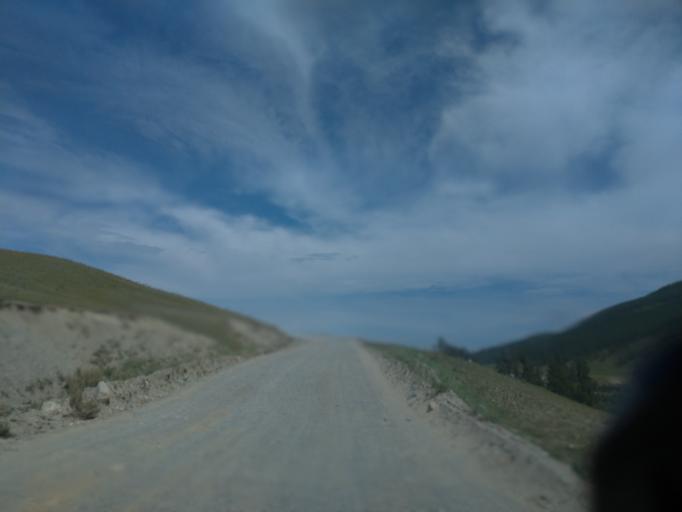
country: RU
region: Altay
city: Ust'-Ulagan
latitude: 50.7089
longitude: 88.0198
